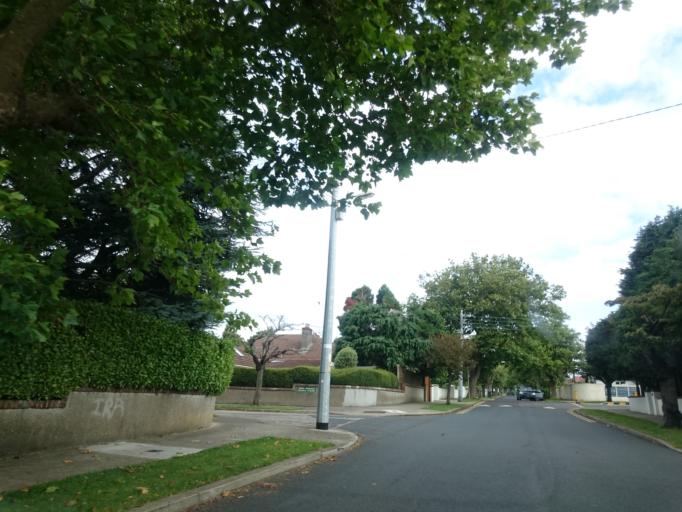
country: IE
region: Leinster
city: Mount Merrion
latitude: 53.2912
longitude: -6.2162
